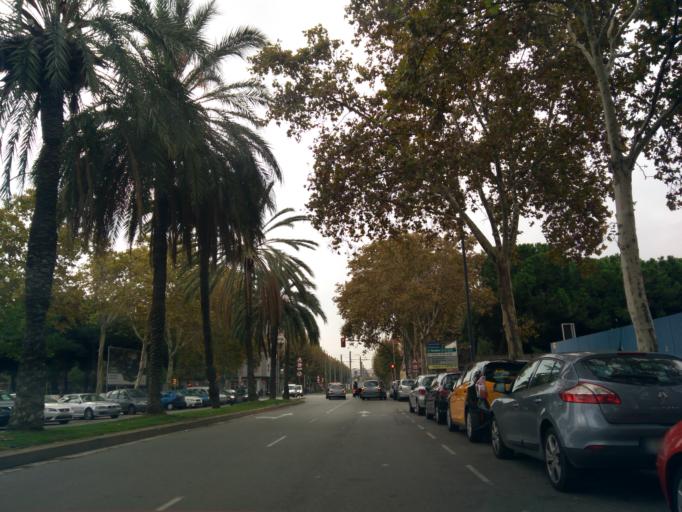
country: ES
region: Catalonia
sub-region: Provincia de Barcelona
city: Sant Adria de Besos
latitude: 41.4277
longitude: 2.2265
